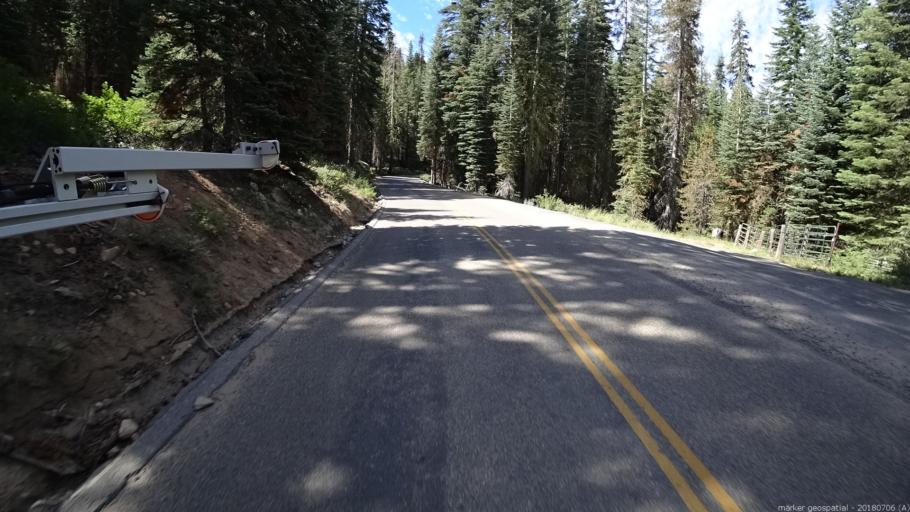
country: US
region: California
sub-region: Madera County
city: Oakhurst
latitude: 37.4338
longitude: -119.4809
